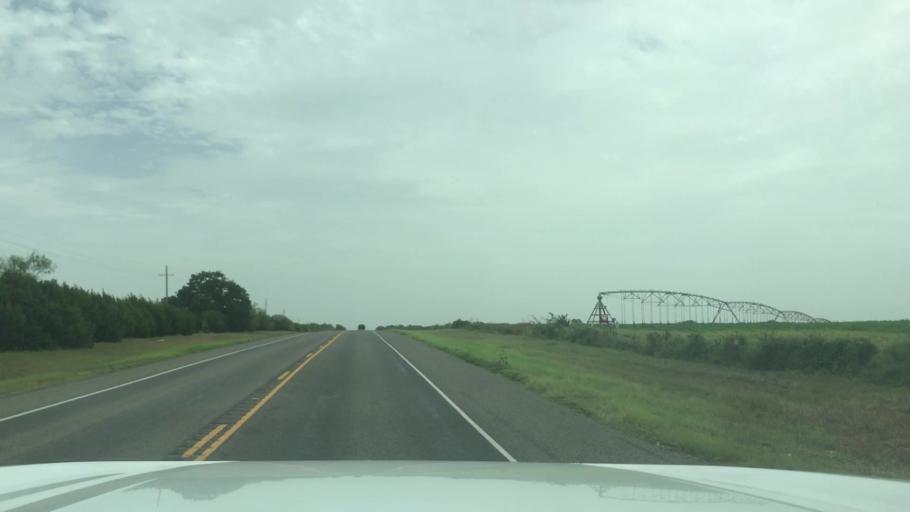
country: US
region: Texas
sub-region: Hamilton County
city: Hico
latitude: 31.9816
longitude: -98.0031
